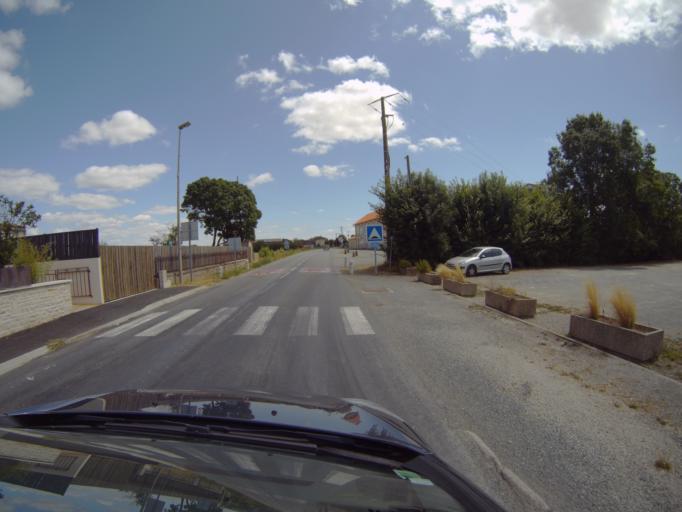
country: FR
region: Poitou-Charentes
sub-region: Departement de la Charente-Maritime
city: Saint-Jean-de-Liversay
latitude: 46.2654
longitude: -0.8749
